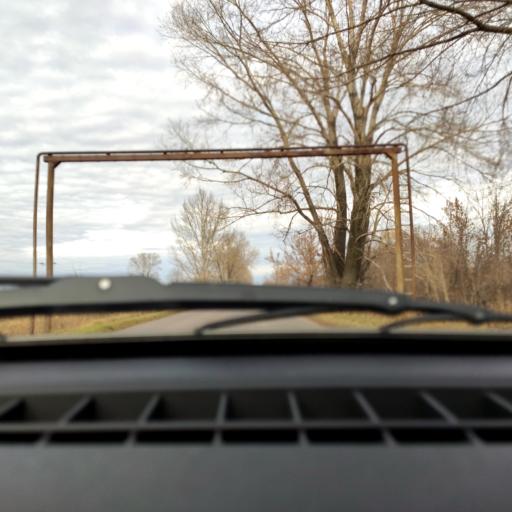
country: RU
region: Bashkortostan
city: Ufa
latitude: 54.8787
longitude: 56.1307
